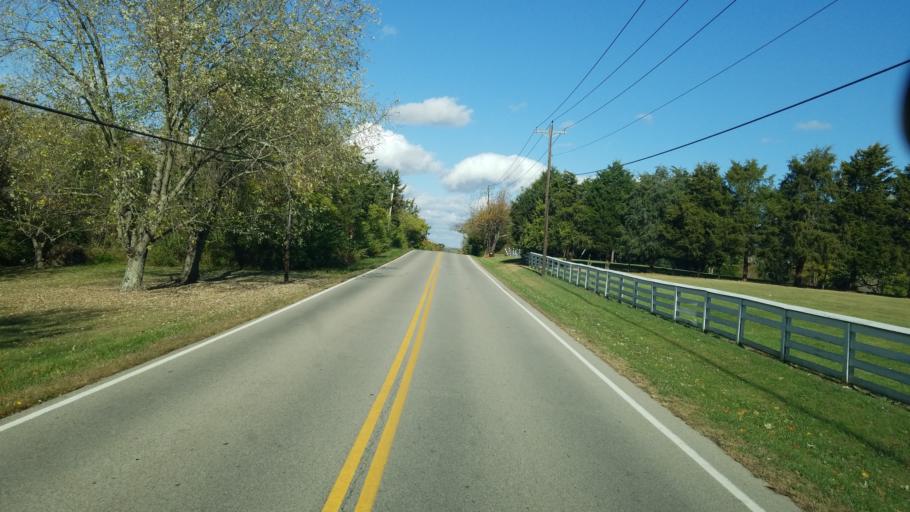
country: US
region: Ohio
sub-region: Warren County
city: Lebanon
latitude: 39.4182
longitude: -84.1848
